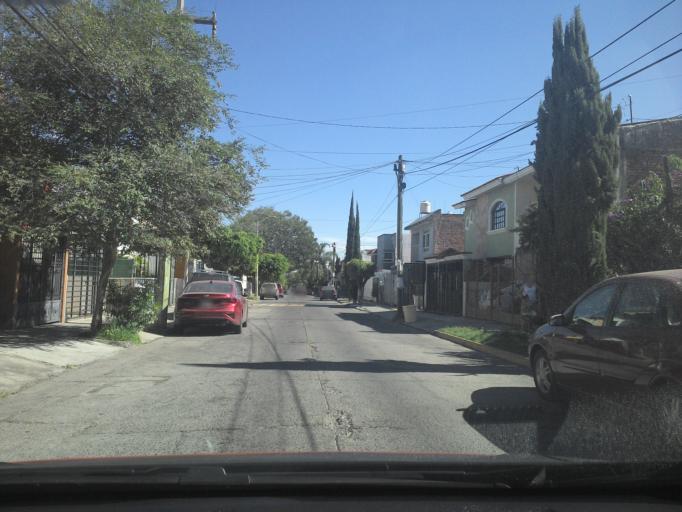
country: MX
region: Jalisco
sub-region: Zapopan
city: Zapopan
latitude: 20.7445
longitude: -103.4034
